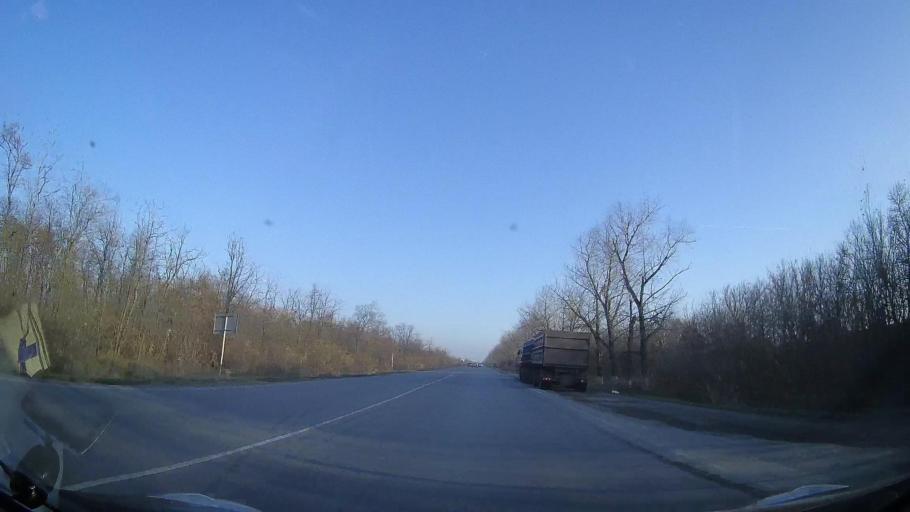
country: RU
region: Rostov
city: Bataysk
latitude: 47.0643
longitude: 39.8089
